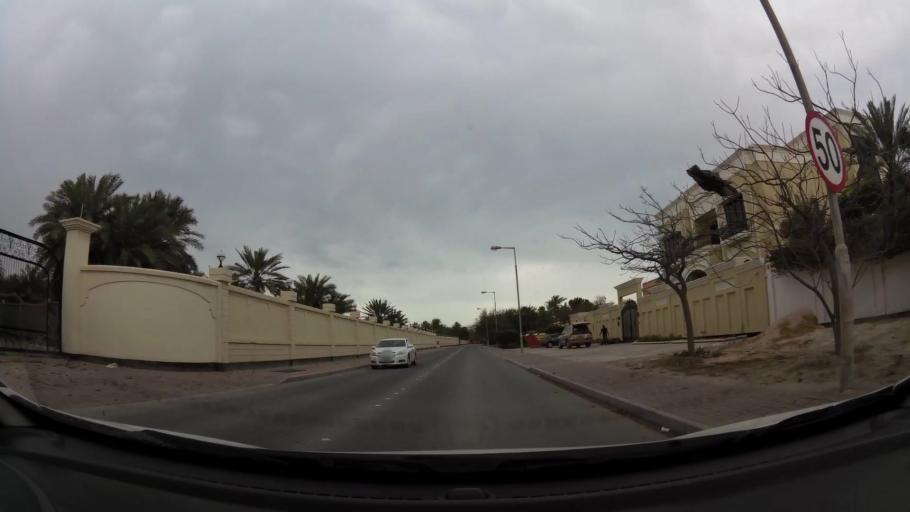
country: BH
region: Central Governorate
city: Madinat Hamad
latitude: 26.1496
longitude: 50.4550
